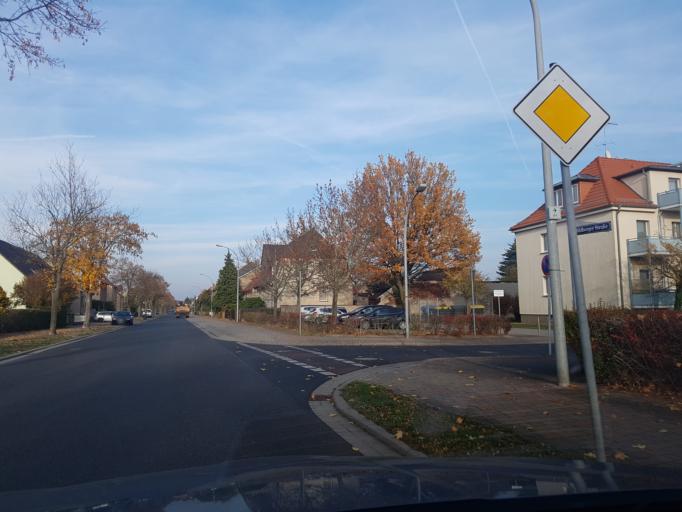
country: DE
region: Brandenburg
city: Falkenberg
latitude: 51.5789
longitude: 13.2319
